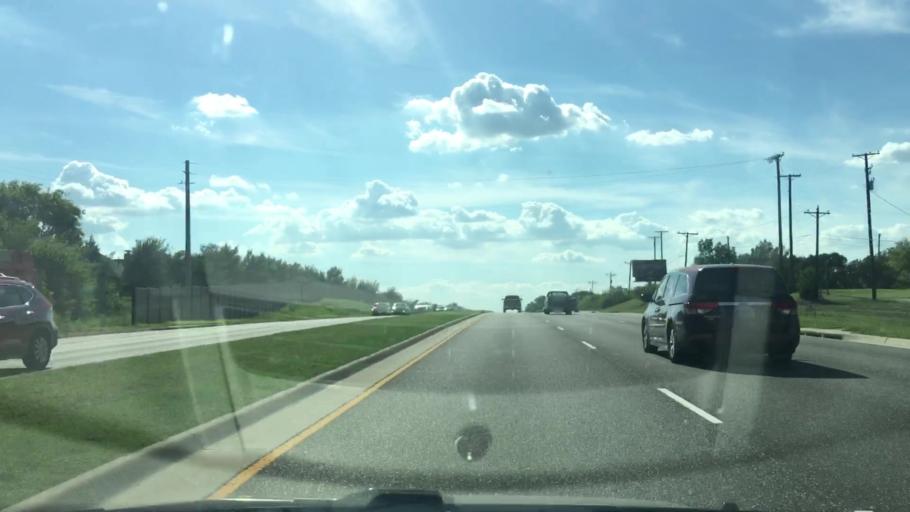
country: US
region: Texas
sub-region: Collin County
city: Prosper
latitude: 33.2193
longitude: -96.7145
